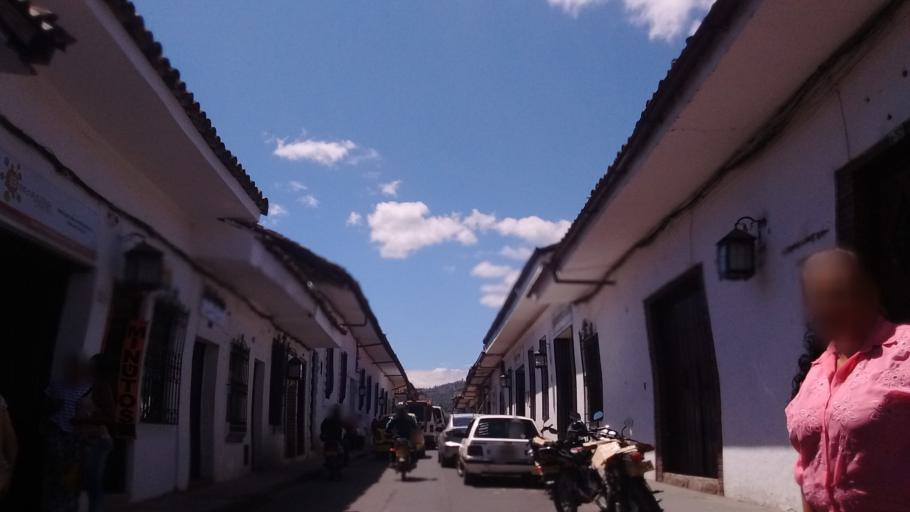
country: CO
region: Cauca
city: Popayan
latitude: 2.4405
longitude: -76.6090
